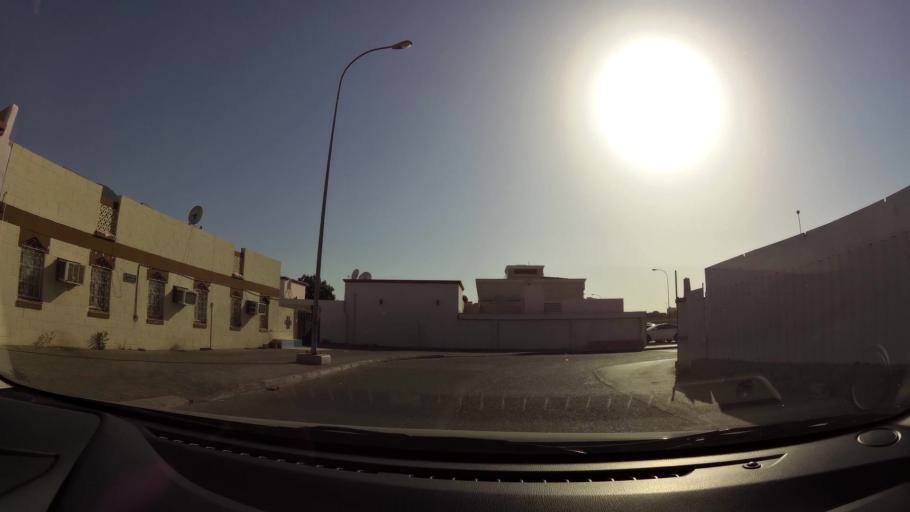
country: OM
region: Muhafazat Masqat
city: As Sib al Jadidah
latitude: 23.6179
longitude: 58.1928
